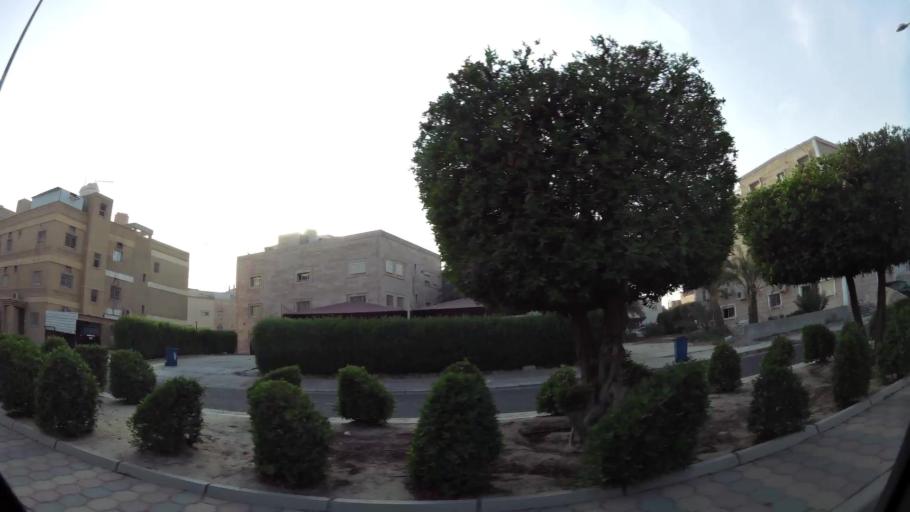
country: KW
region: Mubarak al Kabir
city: Sabah as Salim
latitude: 29.2527
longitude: 48.0712
